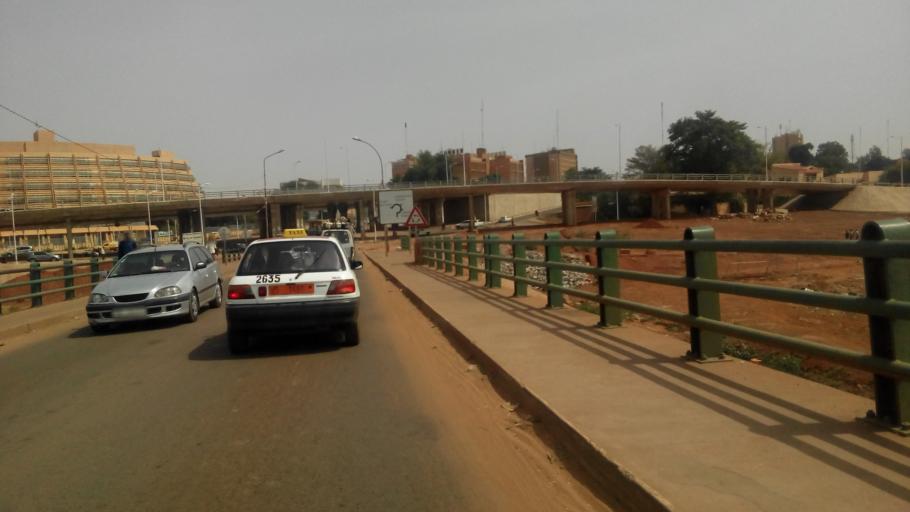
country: NE
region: Niamey
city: Niamey
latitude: 13.5073
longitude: 2.1068
